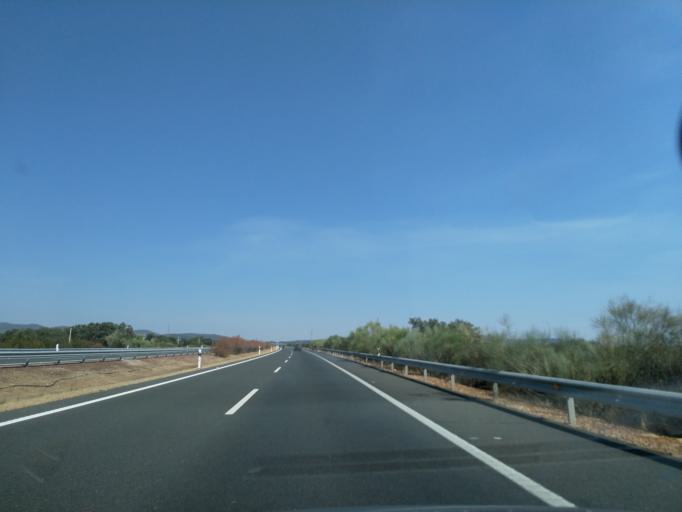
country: ES
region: Extremadura
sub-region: Provincia de Badajoz
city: Carmonita
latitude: 39.1079
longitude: -6.2814
